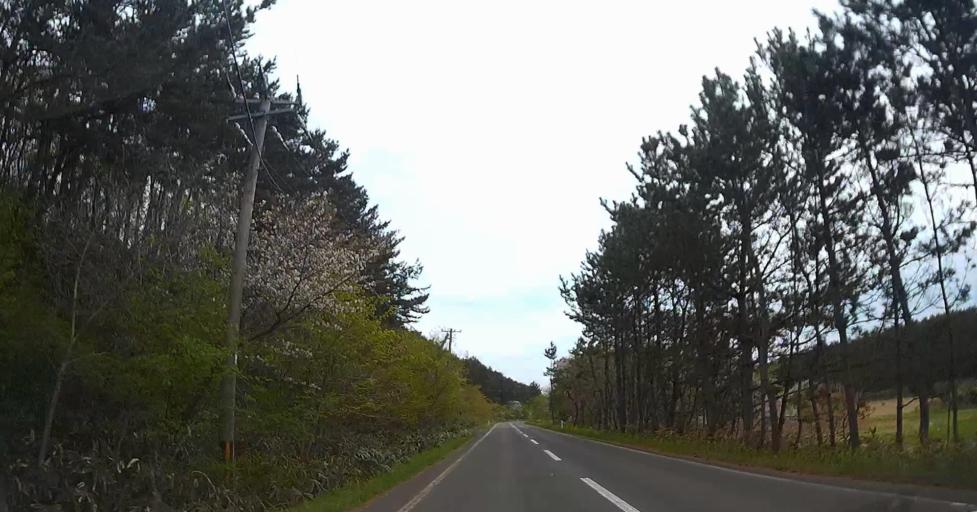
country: JP
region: Aomori
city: Shimokizukuri
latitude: 40.9374
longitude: 140.3230
